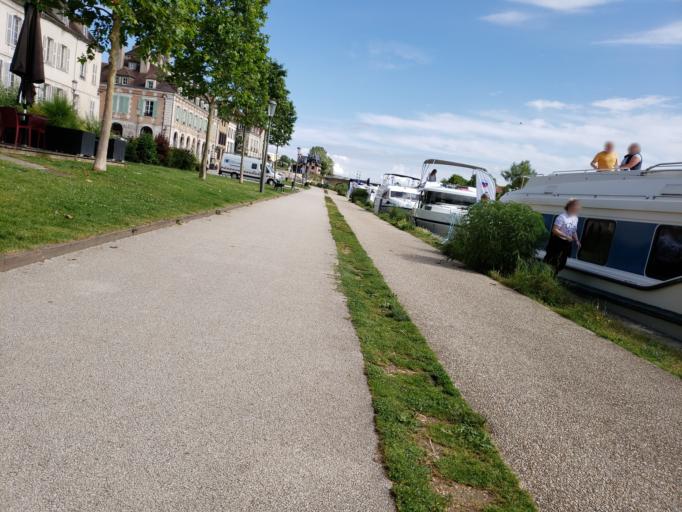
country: FR
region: Bourgogne
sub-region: Departement de l'Yonne
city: Auxerre
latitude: 47.7990
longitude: 3.5746
